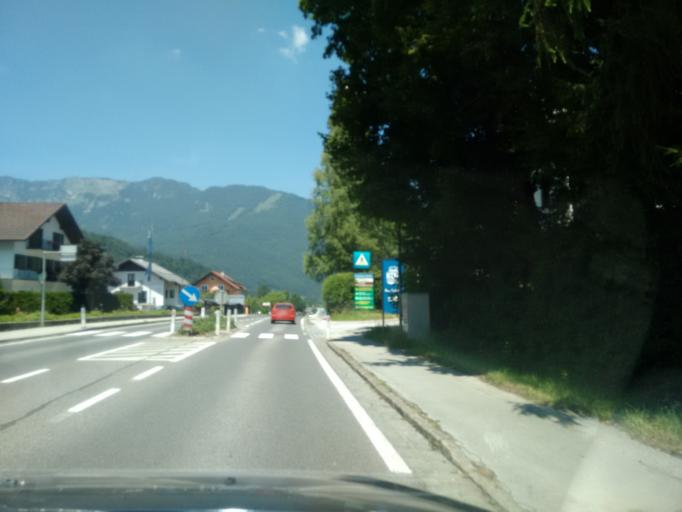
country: AT
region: Upper Austria
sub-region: Politischer Bezirk Gmunden
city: Bad Goisern
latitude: 47.6506
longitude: 13.6122
